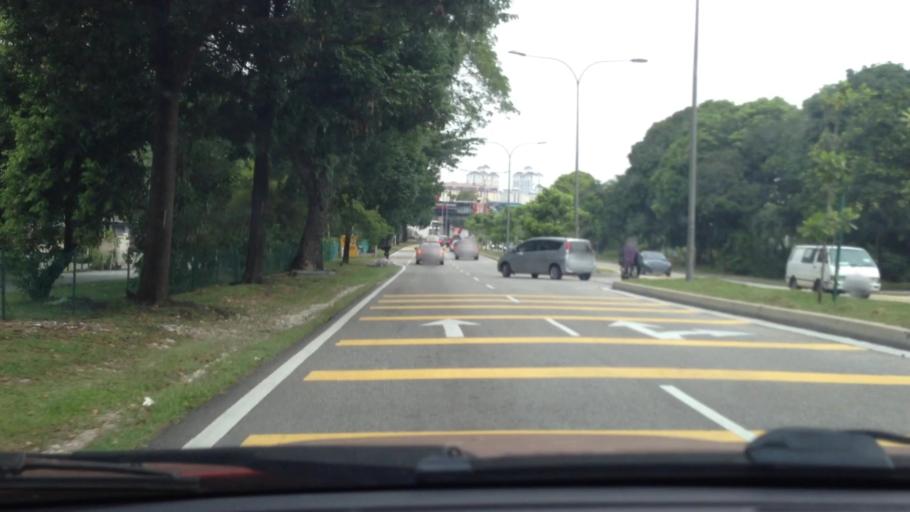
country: MY
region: Selangor
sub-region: Petaling
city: Petaling Jaya
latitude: 3.0937
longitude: 101.6073
